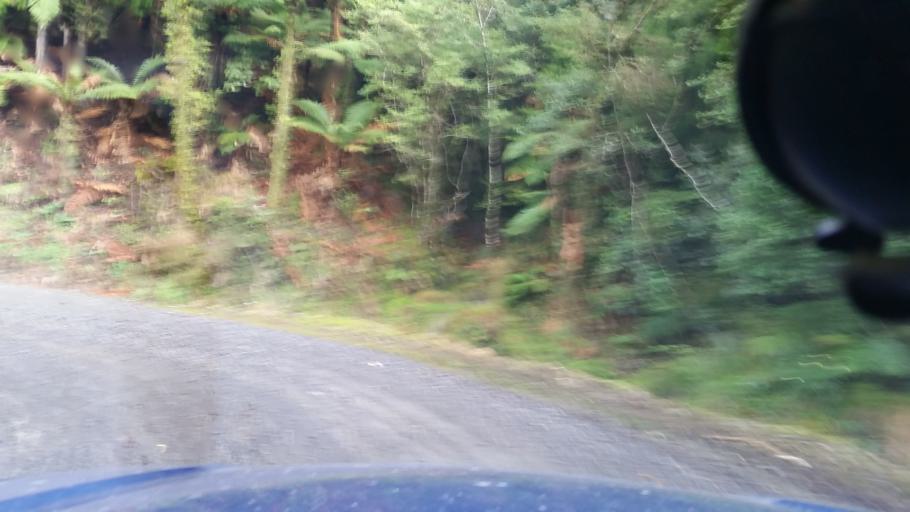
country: NZ
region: Taranaki
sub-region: New Plymouth District
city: Waitara
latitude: -39.0013
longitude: 174.7647
